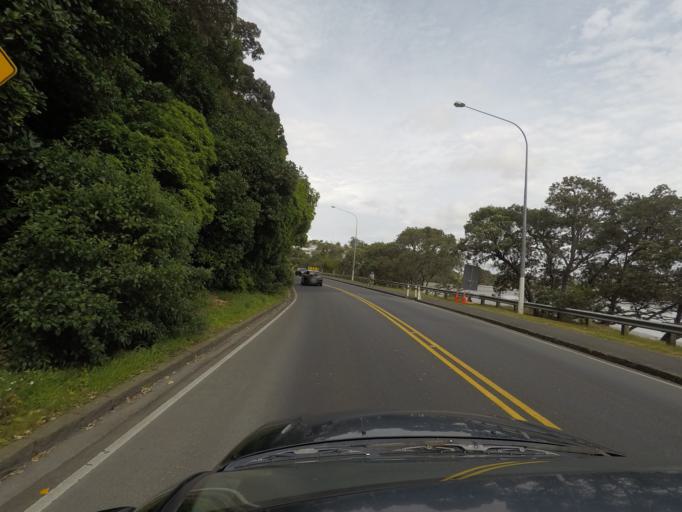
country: NZ
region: Auckland
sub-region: Auckland
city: Auckland
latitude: -36.8545
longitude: 174.8064
